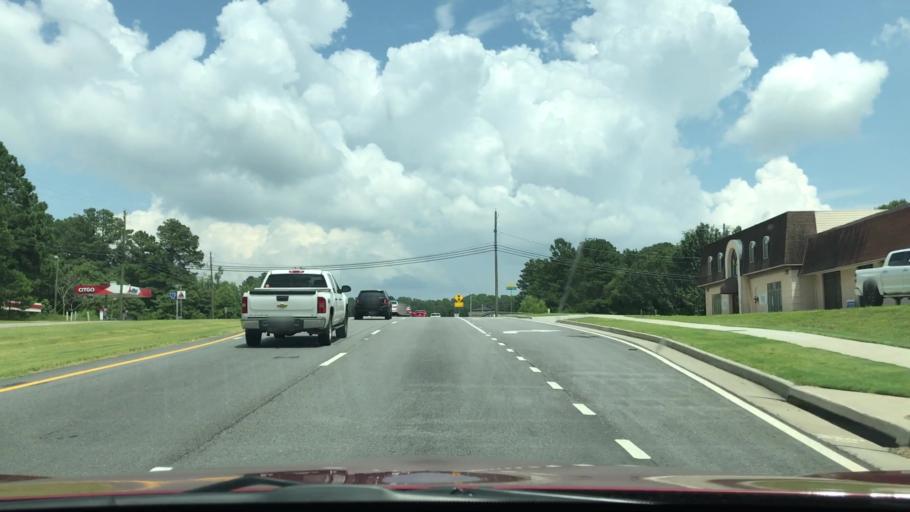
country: US
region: Georgia
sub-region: Gwinnett County
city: Sugar Hill
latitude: 34.1112
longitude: -84.0434
